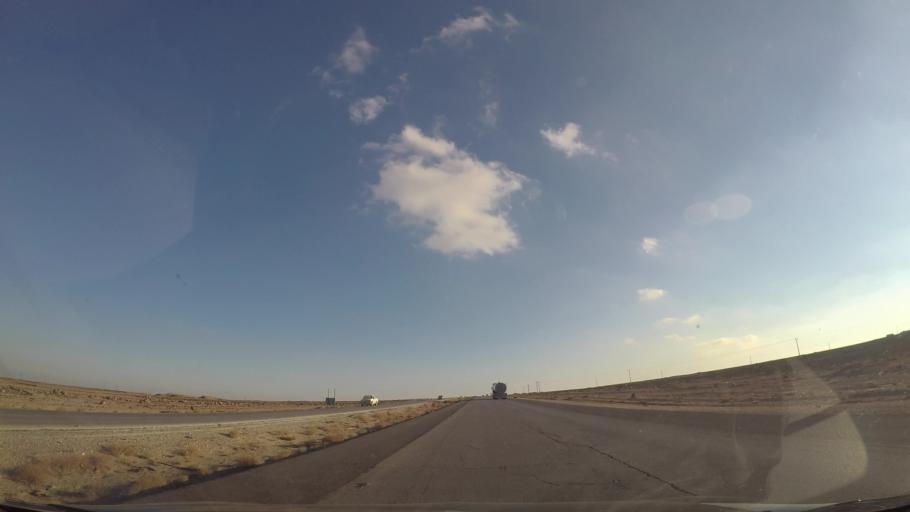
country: JO
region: Tafielah
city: Busayra
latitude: 30.5623
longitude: 35.7985
